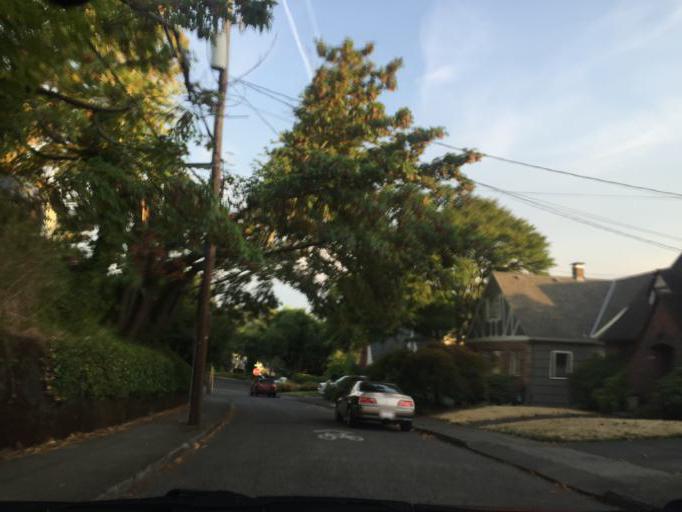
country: US
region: Oregon
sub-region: Multnomah County
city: Portland
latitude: 45.5455
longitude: -122.6244
